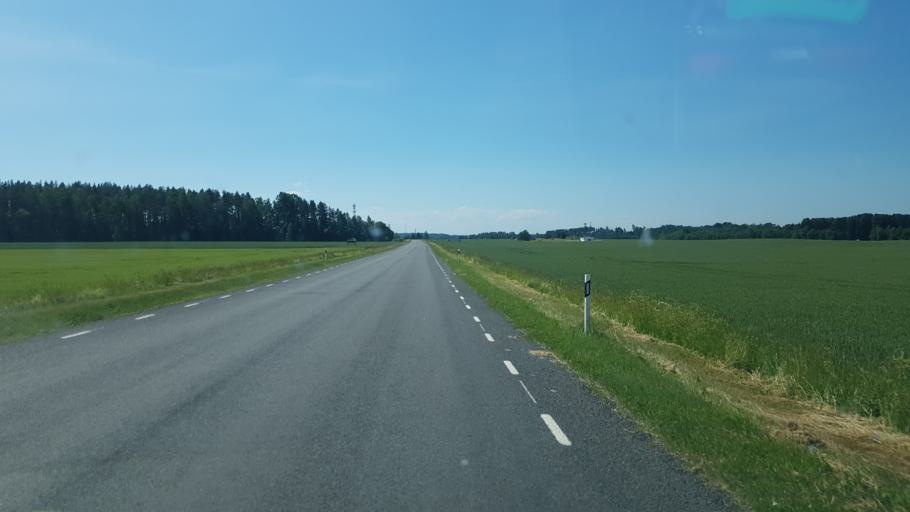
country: EE
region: Tartu
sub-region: UElenurme vald
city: Ulenurme
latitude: 58.3147
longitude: 26.8830
